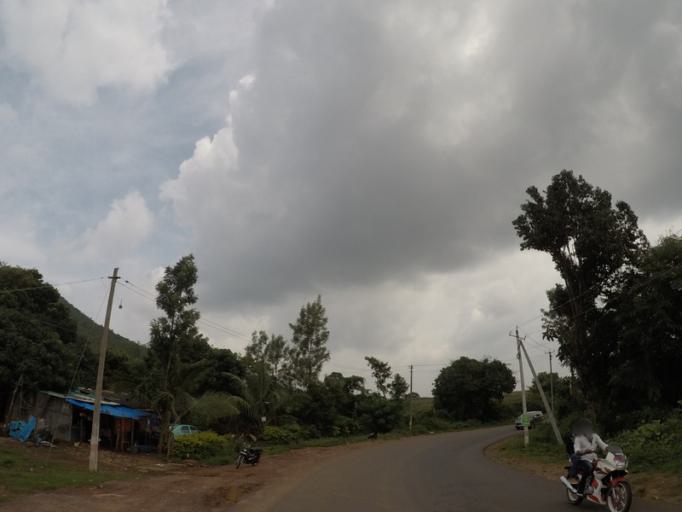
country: IN
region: Karnataka
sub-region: Chikmagalur
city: Chikmagalur
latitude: 13.3662
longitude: 75.7552
